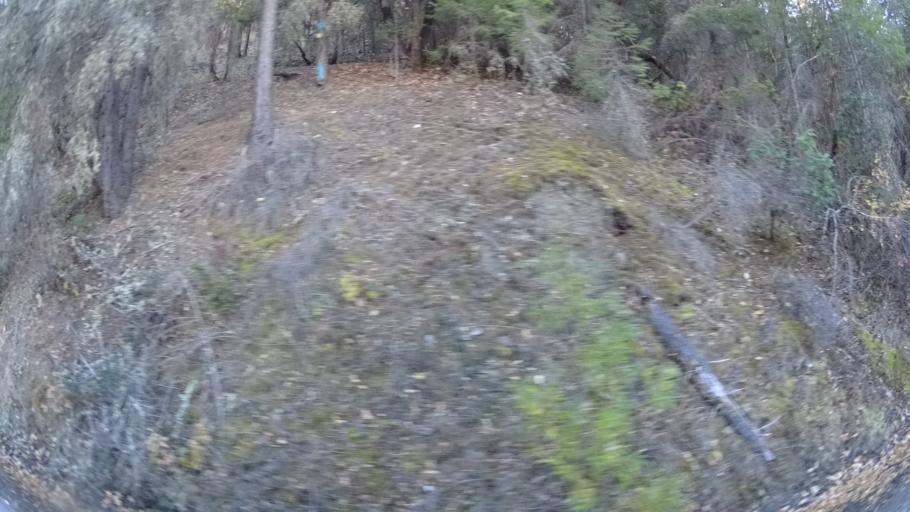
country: US
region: California
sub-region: Siskiyou County
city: Yreka
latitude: 41.8399
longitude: -122.9265
